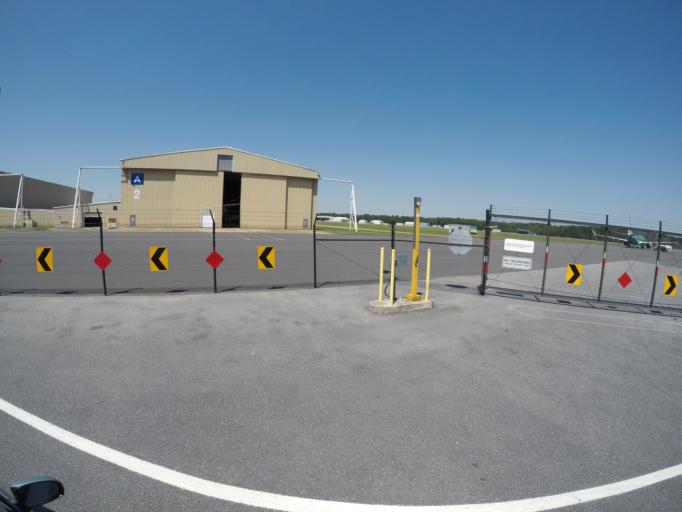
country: US
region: Delaware
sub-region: Sussex County
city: Georgetown
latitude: 38.6917
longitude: -75.3539
